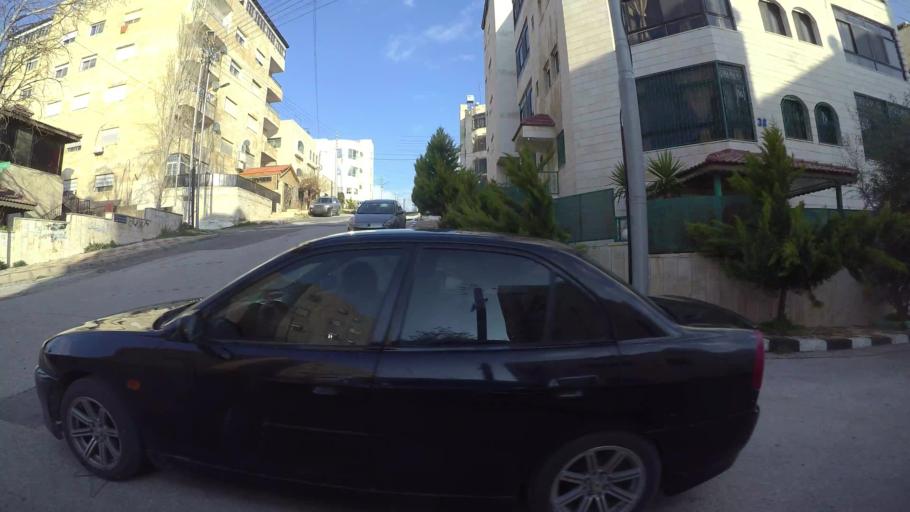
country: JO
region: Amman
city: Al Jubayhah
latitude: 31.9970
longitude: 35.8672
